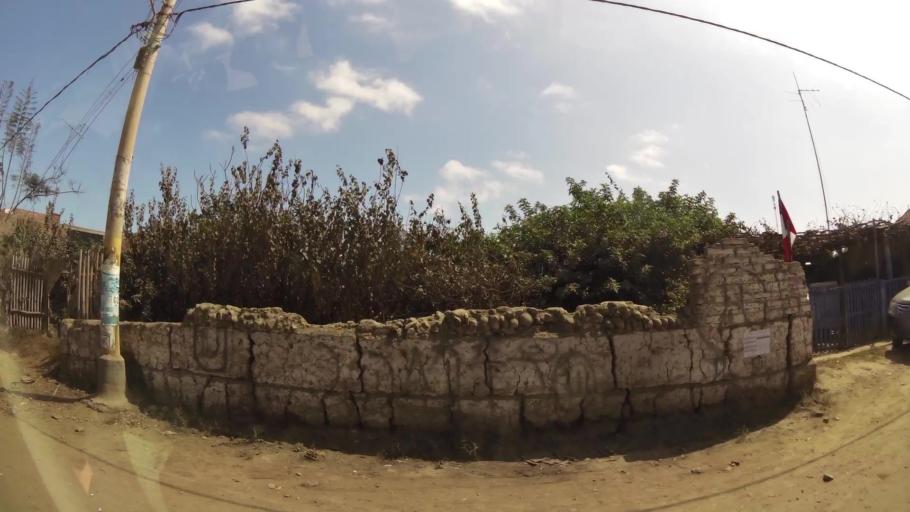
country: PE
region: Lima
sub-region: Provincia de Canete
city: Mala
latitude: -12.6624
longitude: -76.6389
